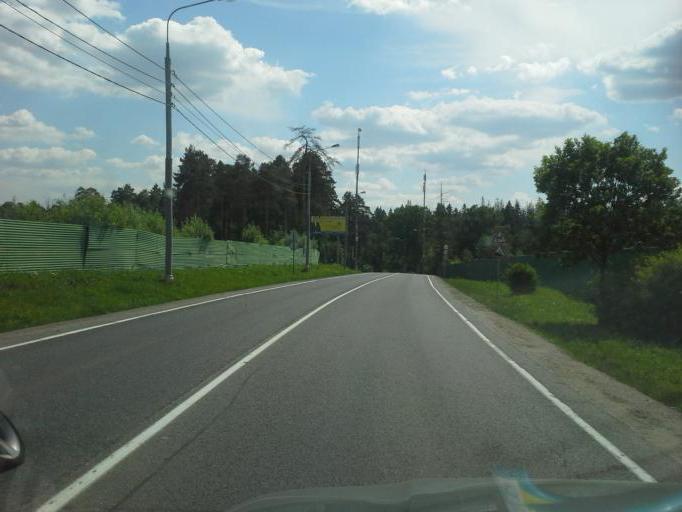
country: RU
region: Moskovskaya
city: Odintsovo
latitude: 55.7098
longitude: 37.2710
